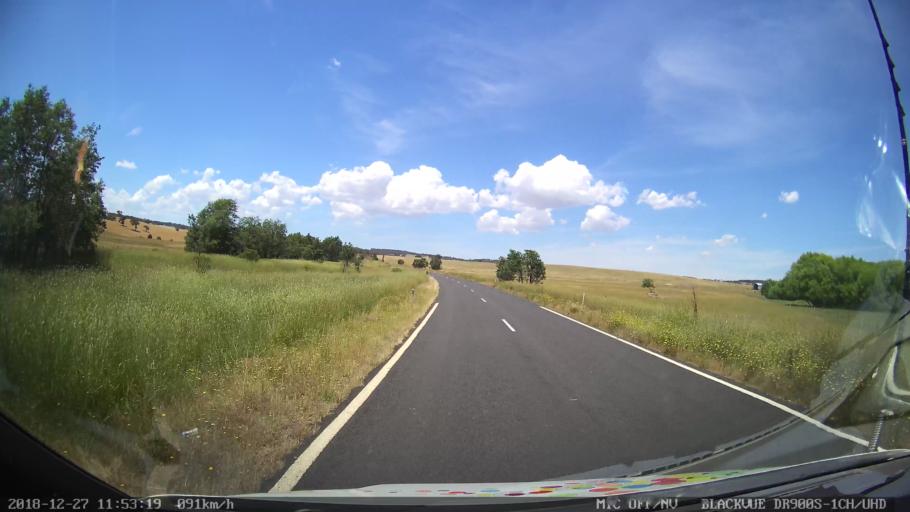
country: AU
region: New South Wales
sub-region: Blayney
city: Blayney
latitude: -33.6603
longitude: 149.4016
